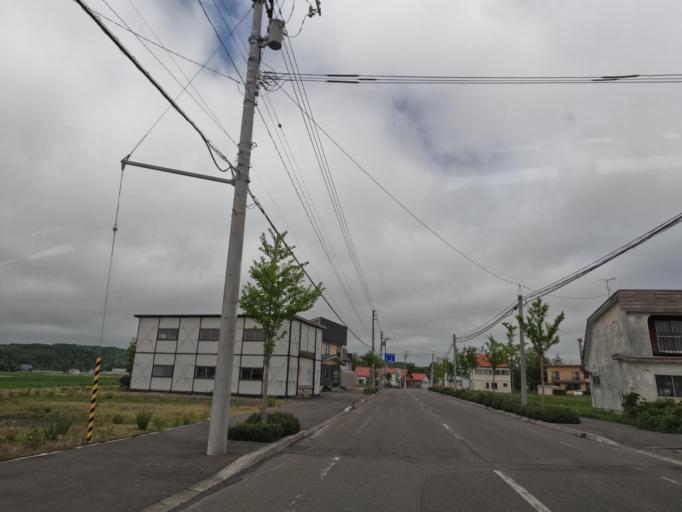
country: JP
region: Hokkaido
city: Tobetsu
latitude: 43.2365
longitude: 141.5137
